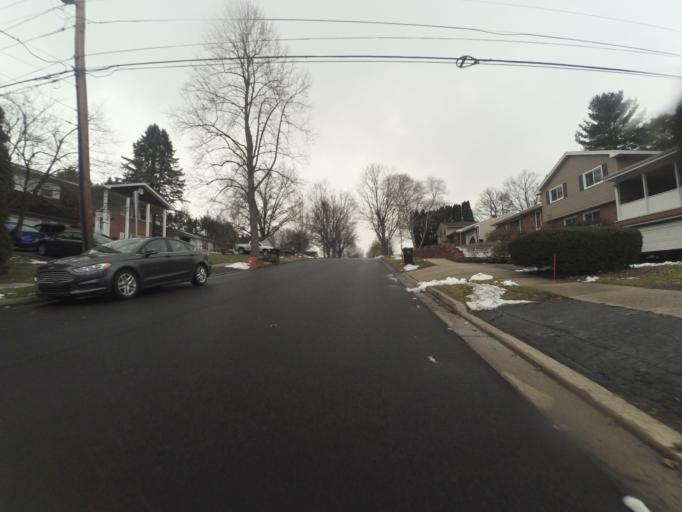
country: US
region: Pennsylvania
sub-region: Centre County
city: State College
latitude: 40.7968
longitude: -77.8444
